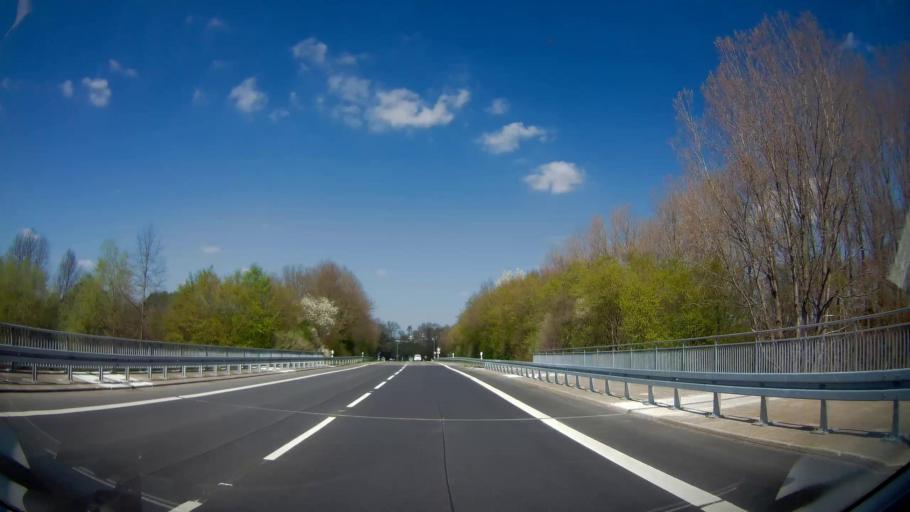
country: DE
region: North Rhine-Westphalia
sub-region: Regierungsbezirk Munster
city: Klein Reken
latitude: 51.7228
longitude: 7.0426
